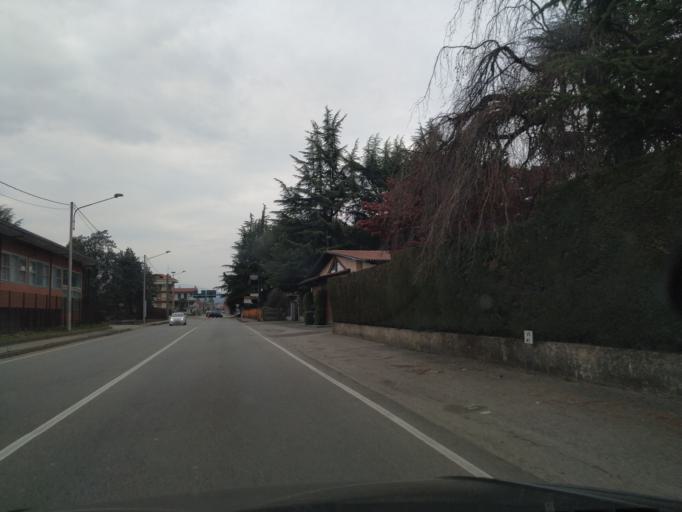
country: IT
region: Piedmont
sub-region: Provincia di Novara
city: Cureggio
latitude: 45.6876
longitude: 8.4569
